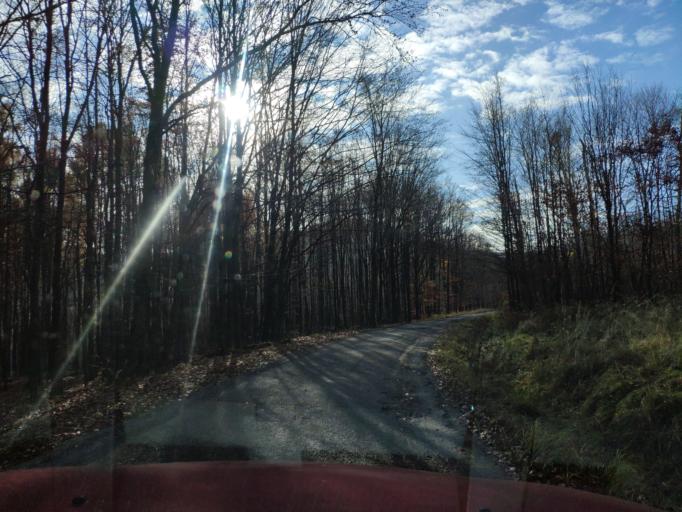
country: HU
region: Borsod-Abauj-Zemplen
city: Gonc
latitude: 48.6011
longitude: 21.4513
